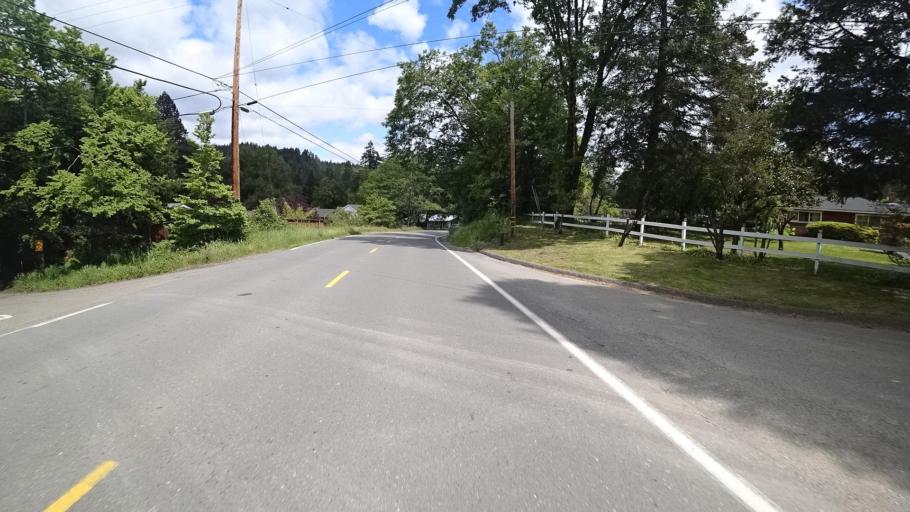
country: US
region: California
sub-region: Humboldt County
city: Redway
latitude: 40.1220
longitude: -123.8310
